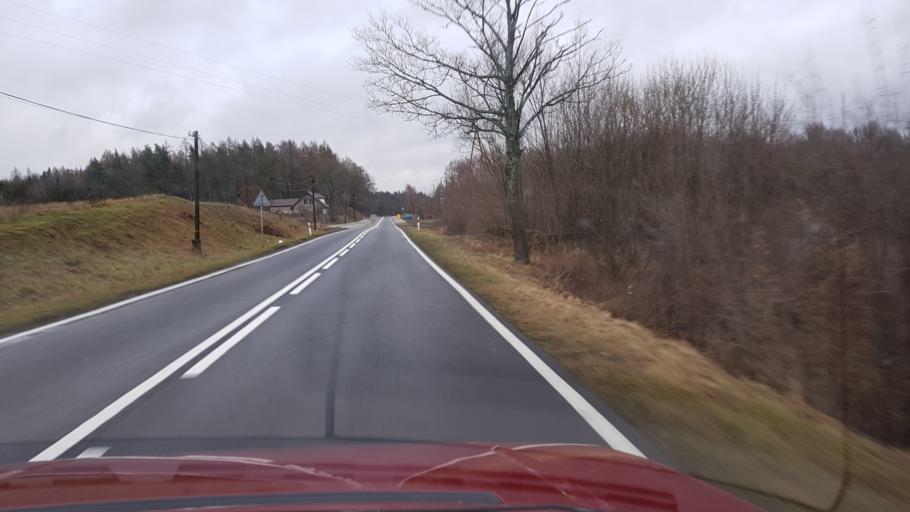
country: PL
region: West Pomeranian Voivodeship
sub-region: Powiat lobeski
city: Wegorzyno
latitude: 53.5210
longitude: 15.6247
